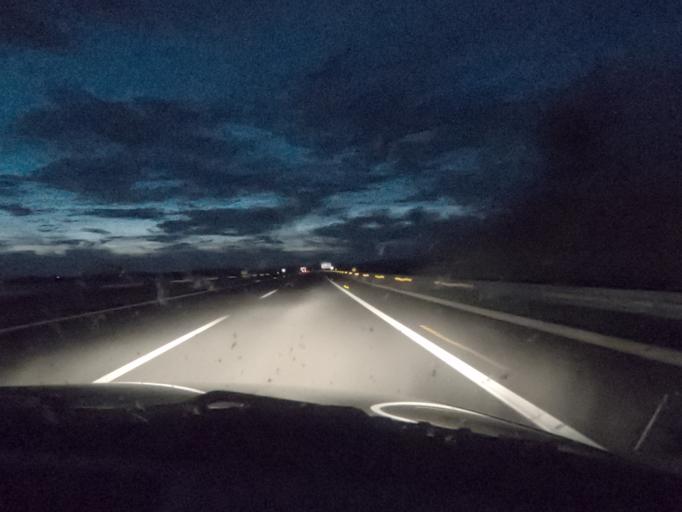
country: ES
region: Extremadura
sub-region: Provincia de Caceres
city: Morcillo
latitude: 39.9769
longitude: -6.3704
